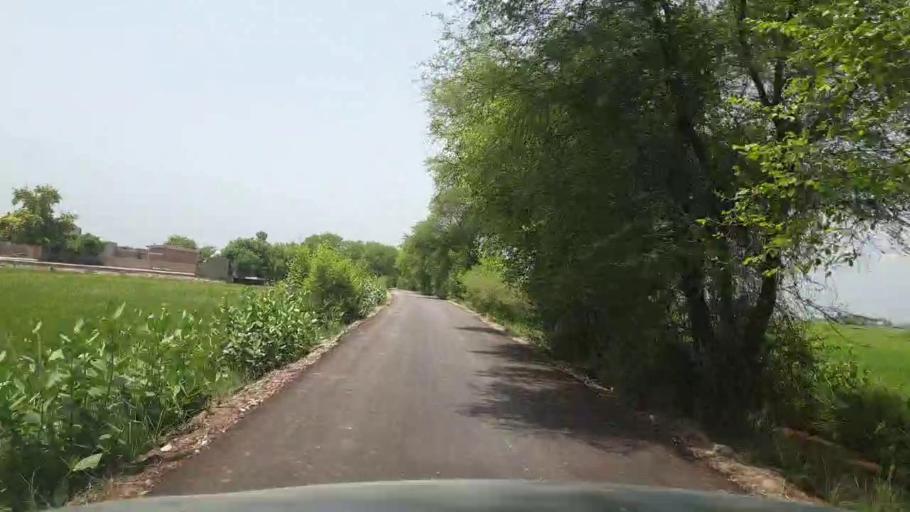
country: PK
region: Sindh
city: Garhi Yasin
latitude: 27.9330
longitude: 68.4285
